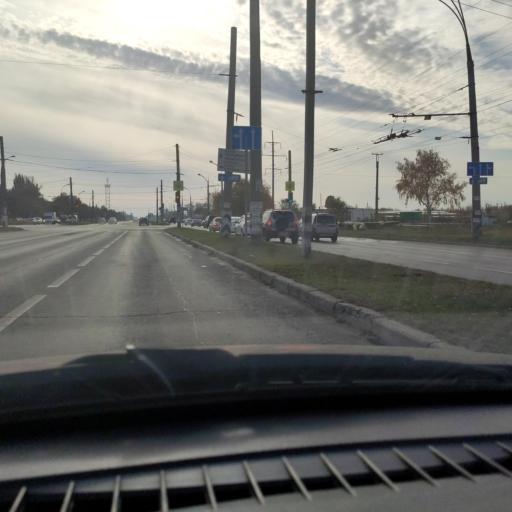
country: RU
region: Samara
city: Tol'yatti
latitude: 53.5402
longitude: 49.2638
